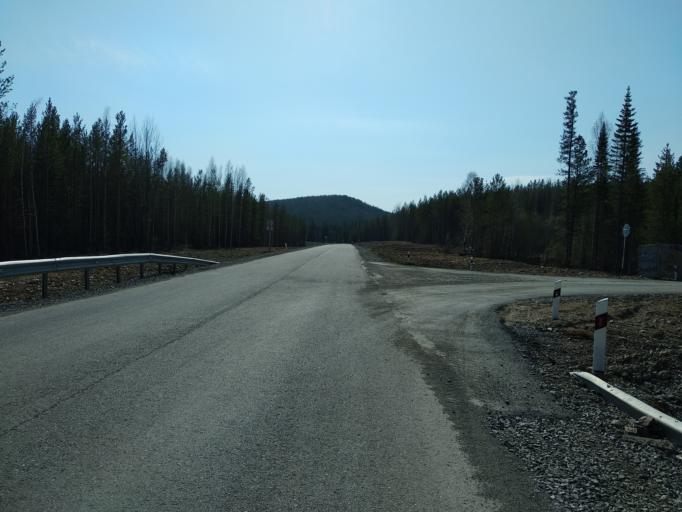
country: RU
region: Sverdlovsk
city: Karpinsk
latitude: 59.5915
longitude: 59.3915
